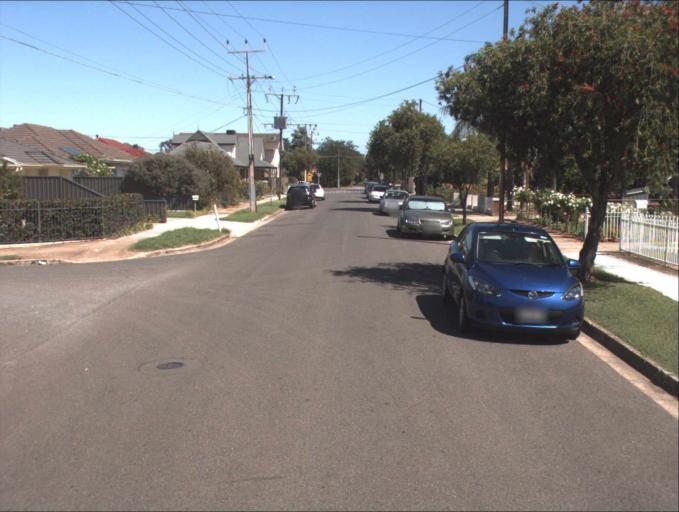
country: AU
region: South Australia
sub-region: Port Adelaide Enfield
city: Klemzig
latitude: -34.8839
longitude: 138.6391
